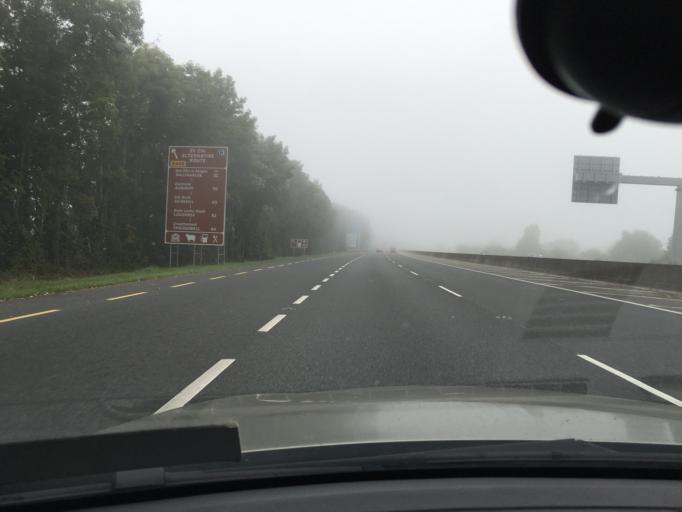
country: IE
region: Leinster
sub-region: An Iarmhi
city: Athlone
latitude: 53.4261
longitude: -7.9686
